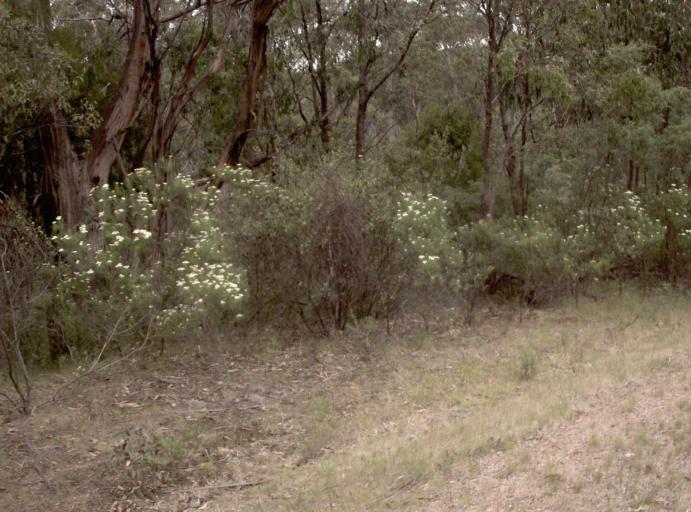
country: AU
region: Victoria
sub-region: East Gippsland
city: Bairnsdale
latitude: -37.6099
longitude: 147.1900
